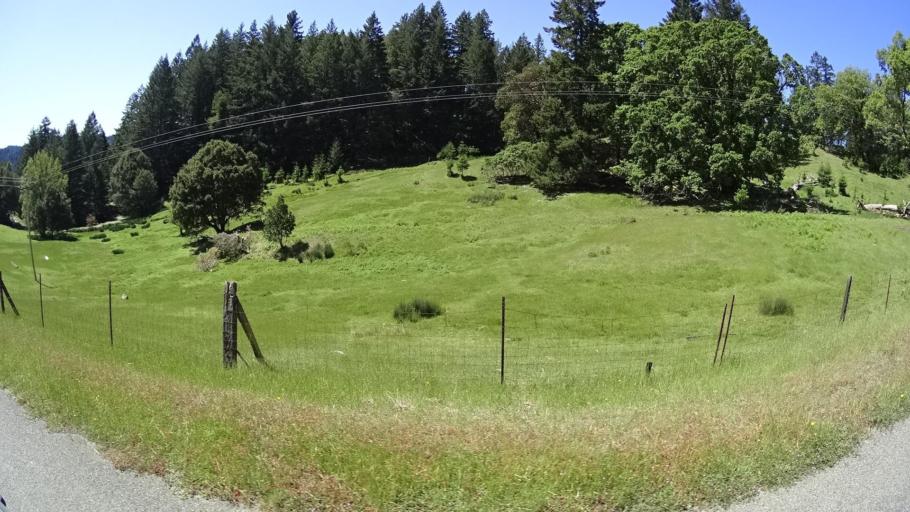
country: US
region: California
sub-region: Humboldt County
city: Redway
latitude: 40.1429
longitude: -124.0065
